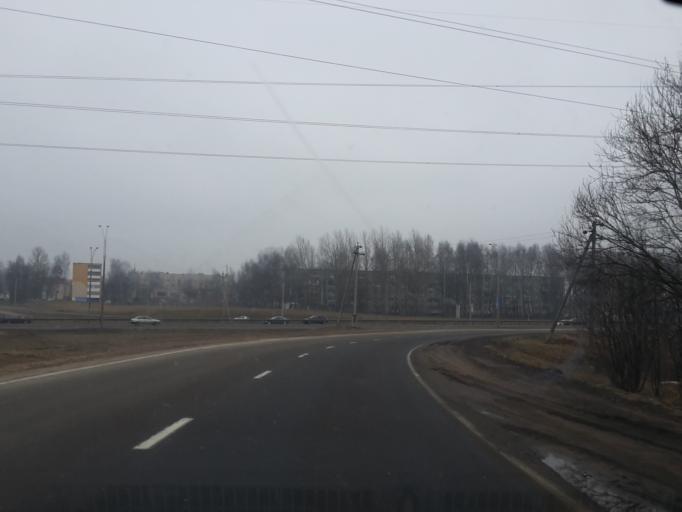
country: BY
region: Minsk
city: Zhdanovichy
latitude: 53.9103
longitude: 27.4074
